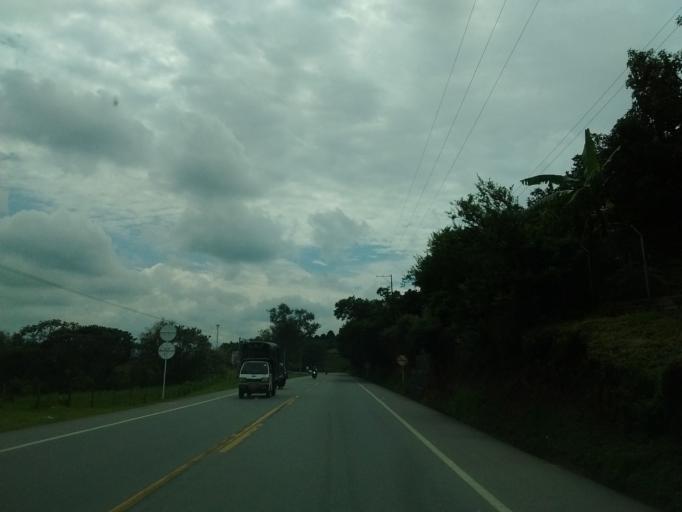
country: CO
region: Cauca
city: Cajibio
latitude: 2.5474
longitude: -76.5624
